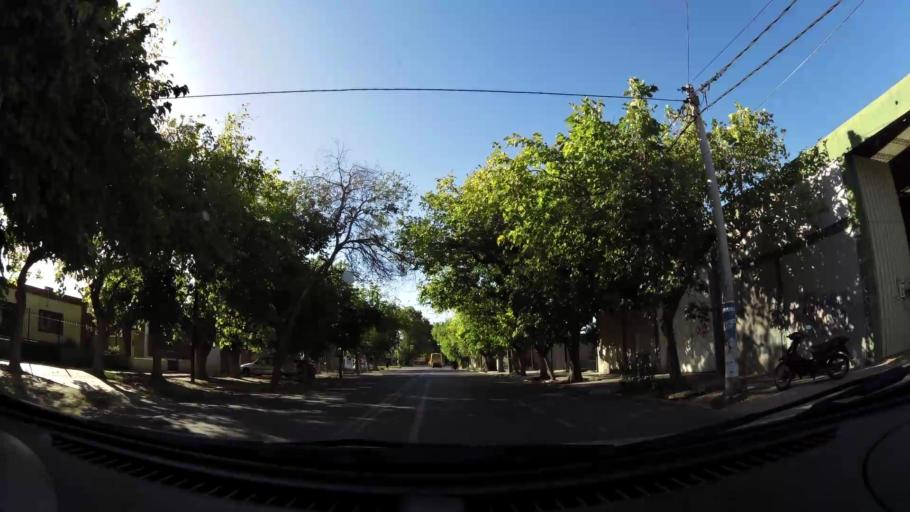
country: AR
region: San Juan
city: Villa Krause
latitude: -31.5657
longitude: -68.5211
